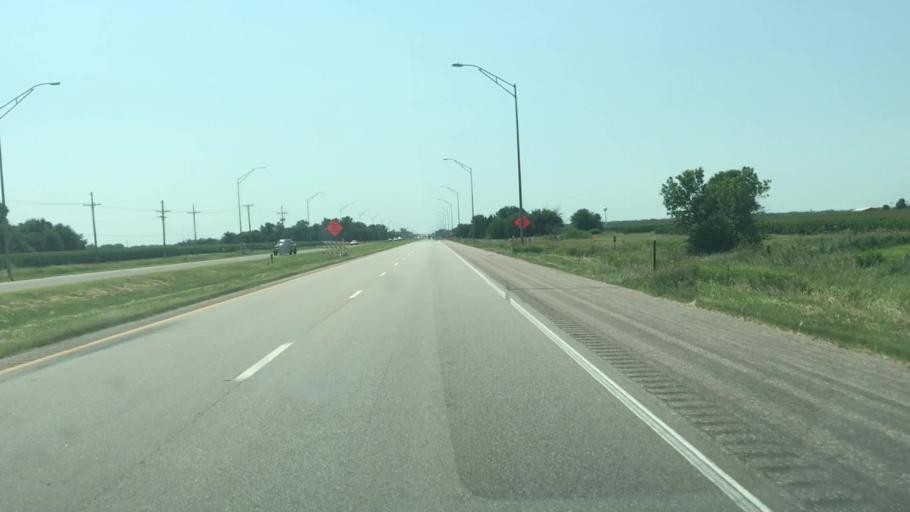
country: US
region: Nebraska
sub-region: Hall County
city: Grand Island
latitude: 40.8507
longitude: -98.3786
